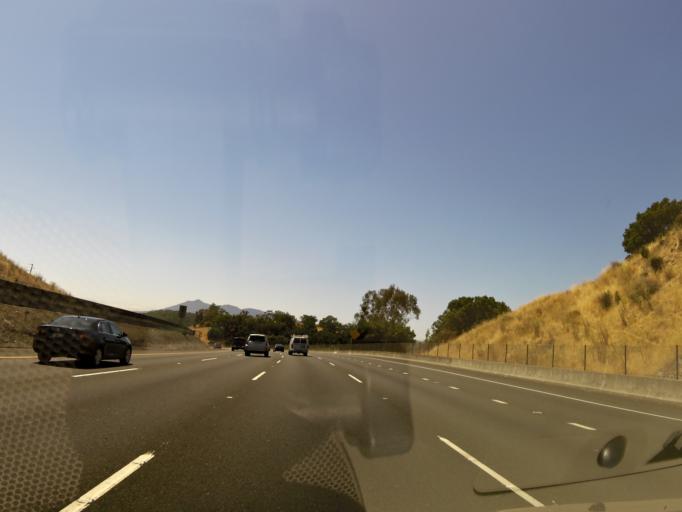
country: US
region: California
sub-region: Marin County
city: Lucas Valley-Marinwood
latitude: 38.0426
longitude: -122.5365
